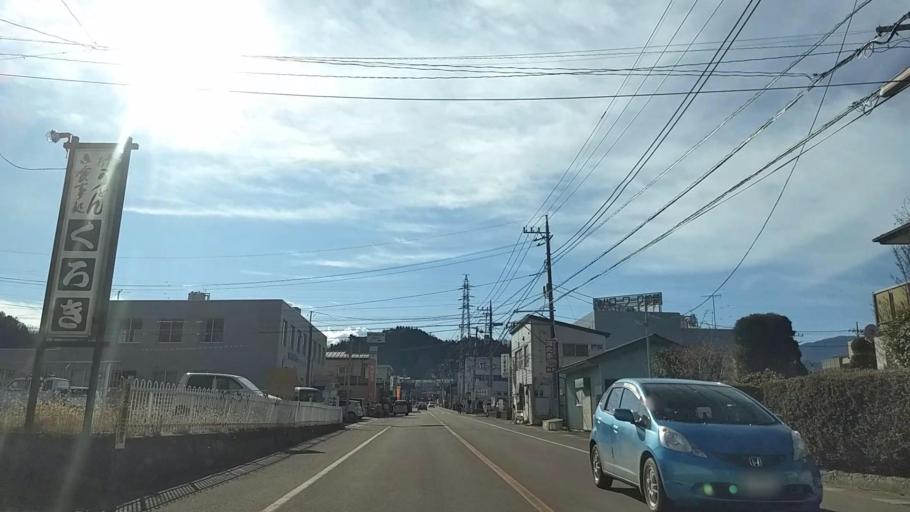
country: JP
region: Yamanashi
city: Otsuki
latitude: 35.5618
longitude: 138.9116
